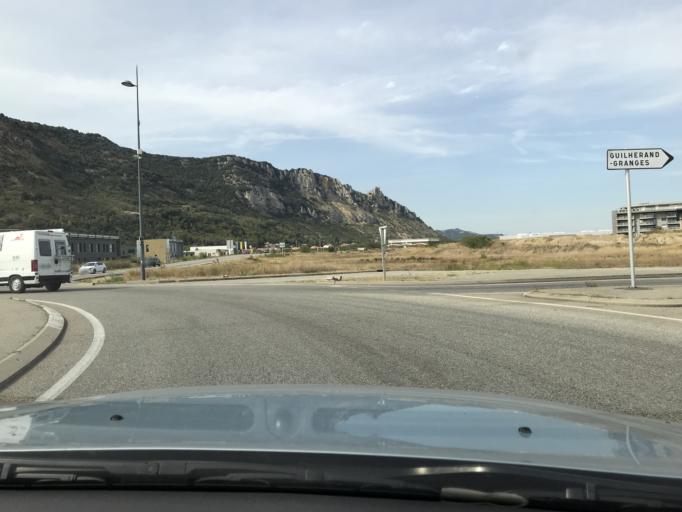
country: FR
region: Rhone-Alpes
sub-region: Departement de l'Ardeche
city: Guilherand-Granges
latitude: 44.9207
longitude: 4.8626
